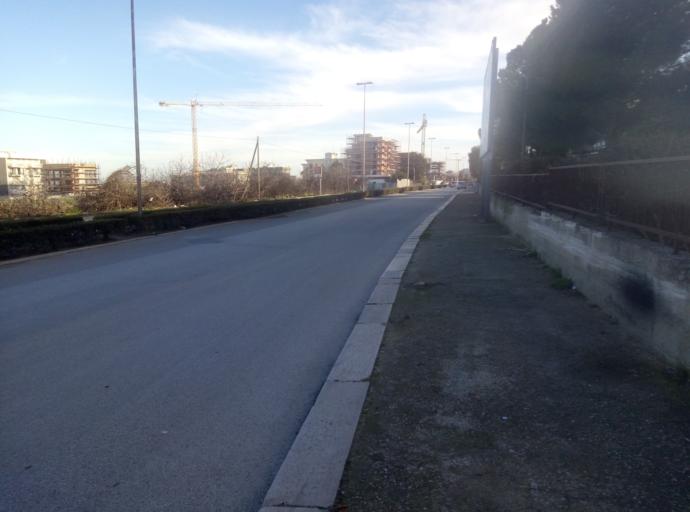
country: IT
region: Apulia
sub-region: Provincia di Bari
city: Ruvo di Puglia
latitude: 41.1219
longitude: 16.4902
